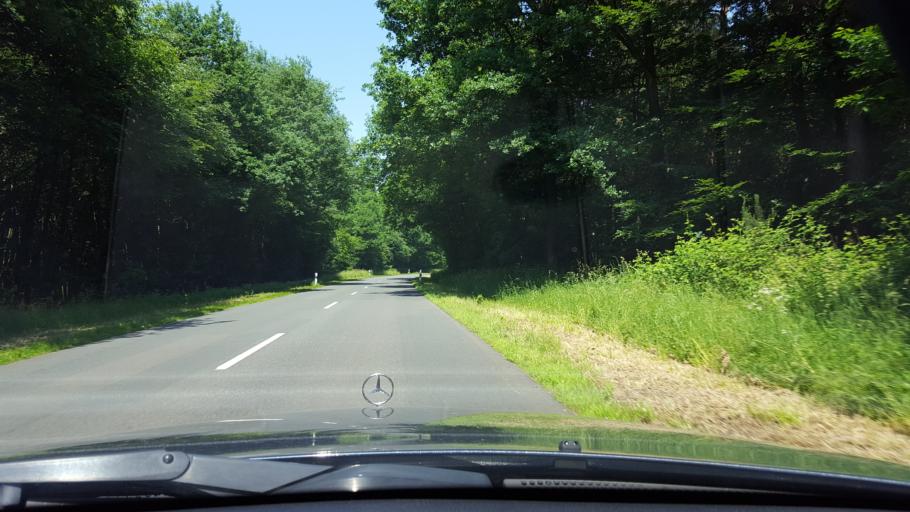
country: DE
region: North Rhine-Westphalia
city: Olfen
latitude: 51.7062
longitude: 7.3152
